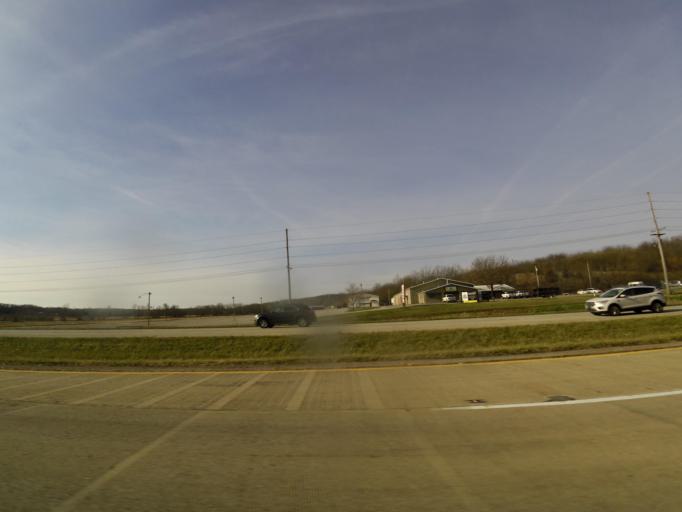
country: US
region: Illinois
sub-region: De Witt County
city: Clinton
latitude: 40.1083
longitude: -88.9652
